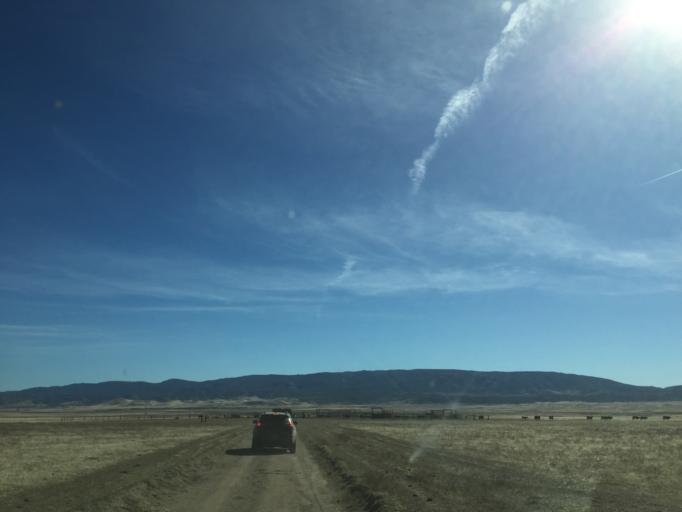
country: US
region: California
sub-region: Kern County
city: Lebec
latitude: 34.8509
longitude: -118.6688
